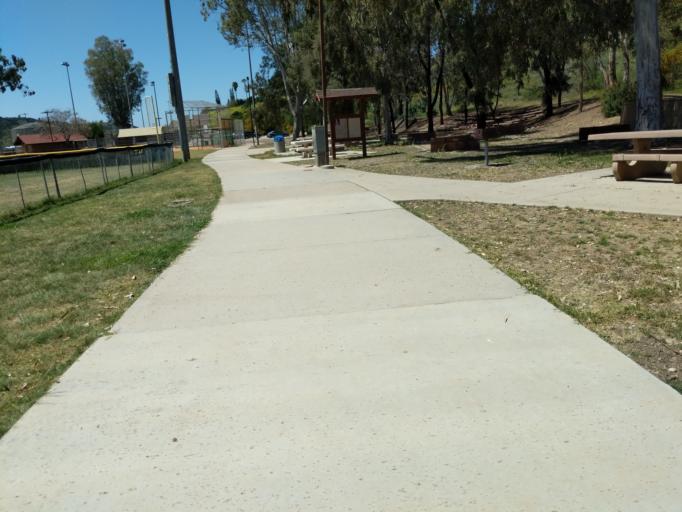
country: US
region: California
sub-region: San Diego County
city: Fairbanks Ranch
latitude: 32.9426
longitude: -117.1322
